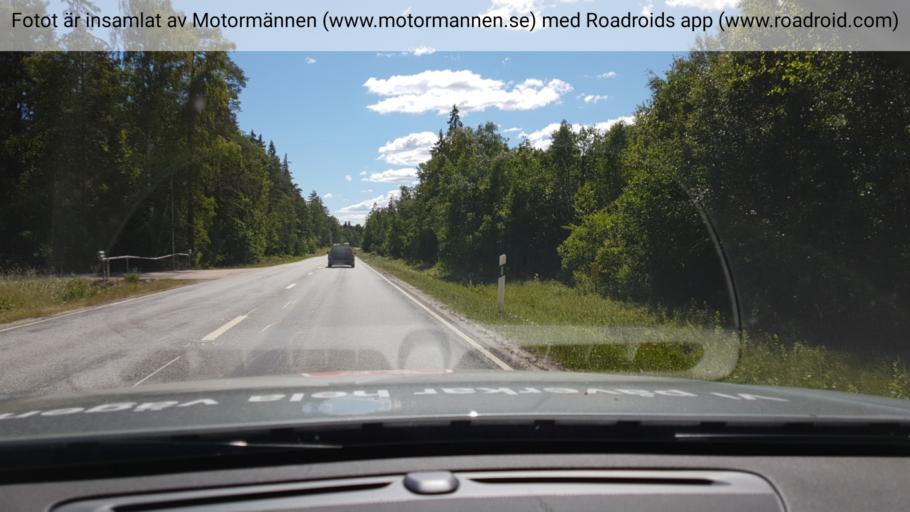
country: SE
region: Soedermanland
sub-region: Strangnas Kommun
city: Strangnas
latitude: 59.3254
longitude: 17.0129
